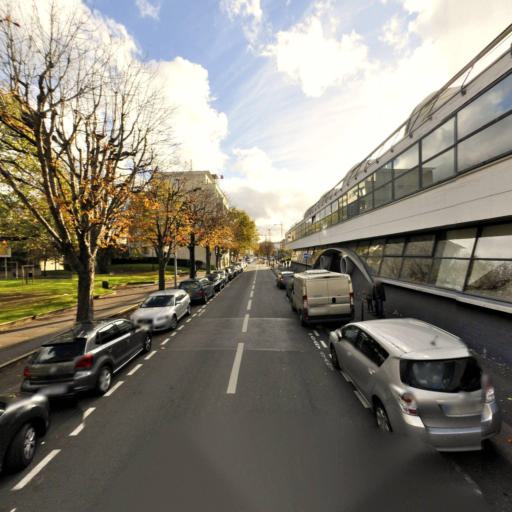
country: FR
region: Ile-de-France
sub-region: Departement des Hauts-de-Seine
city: Boulogne-Billancourt
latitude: 48.8305
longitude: 2.2422
